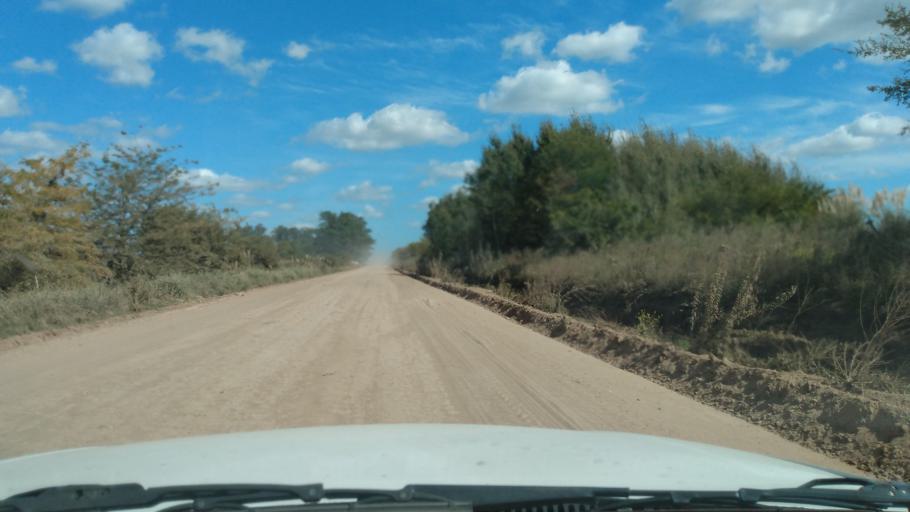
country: AR
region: Buenos Aires
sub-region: Partido de Navarro
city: Navarro
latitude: -35.0225
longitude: -59.4341
